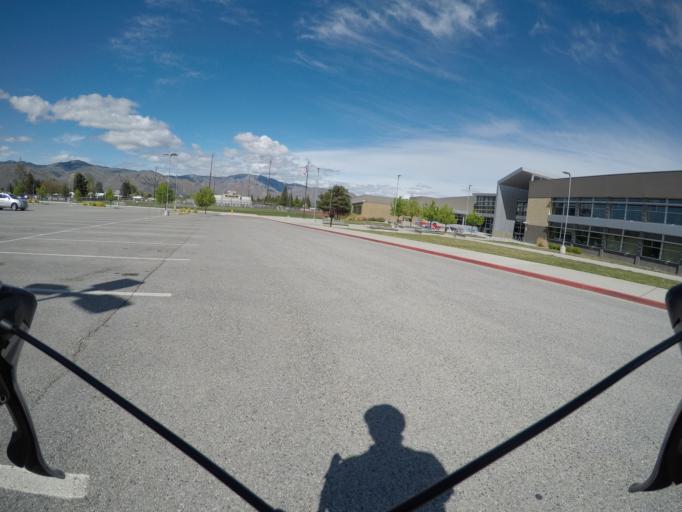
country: US
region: Washington
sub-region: Douglas County
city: East Wenatchee Bench
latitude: 47.4105
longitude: -120.2728
